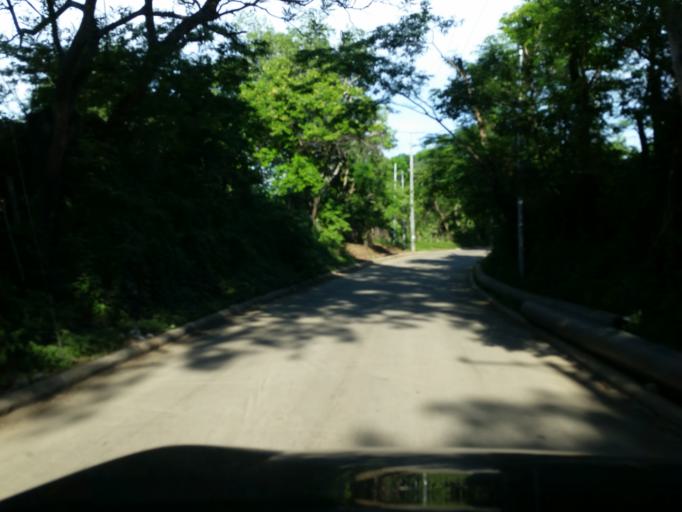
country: NI
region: Managua
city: Managua
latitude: 12.1014
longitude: -86.2174
